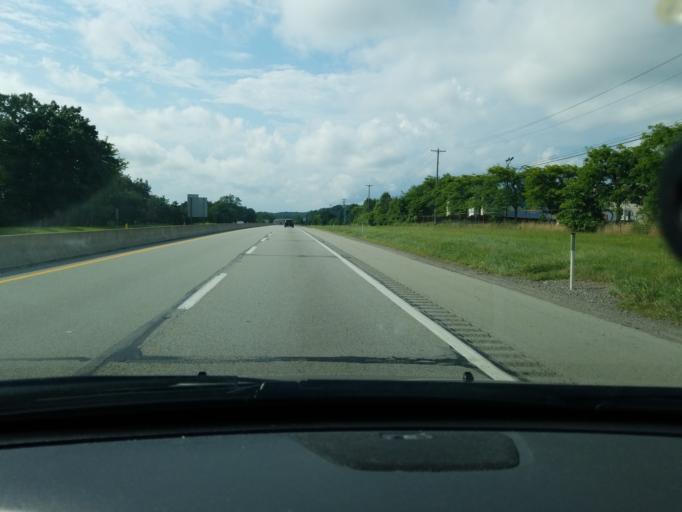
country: US
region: Pennsylvania
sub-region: Butler County
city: Cranberry Township
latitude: 40.6933
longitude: -80.1140
